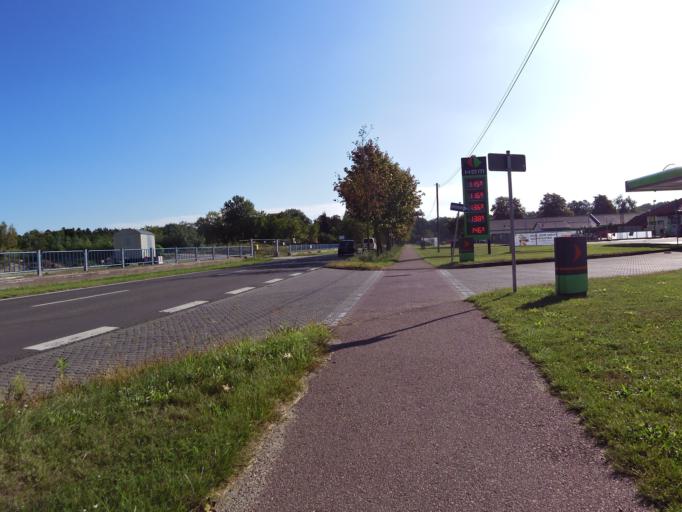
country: DE
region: Saxony-Anhalt
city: Aken
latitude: 51.8506
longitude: 12.0887
